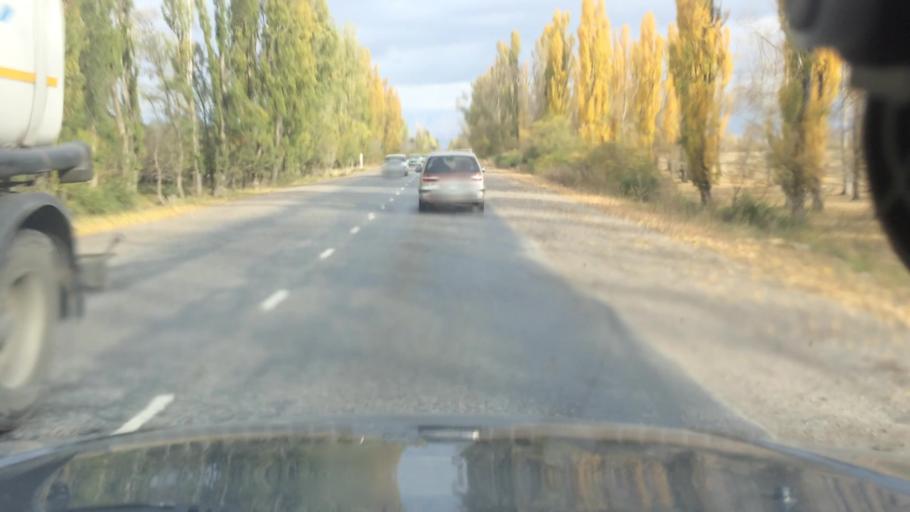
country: KG
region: Ysyk-Koel
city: Tyup
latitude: 42.6150
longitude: 78.3656
